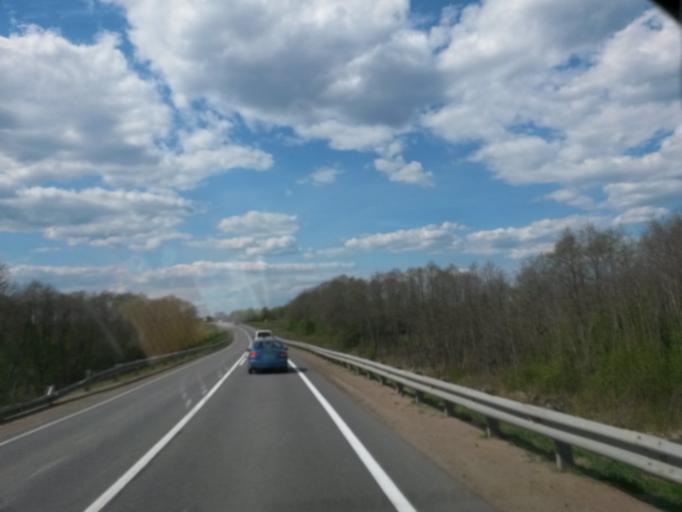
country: RU
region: Jaroslavl
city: Bol'shoye Selo
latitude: 57.7267
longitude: 38.9119
